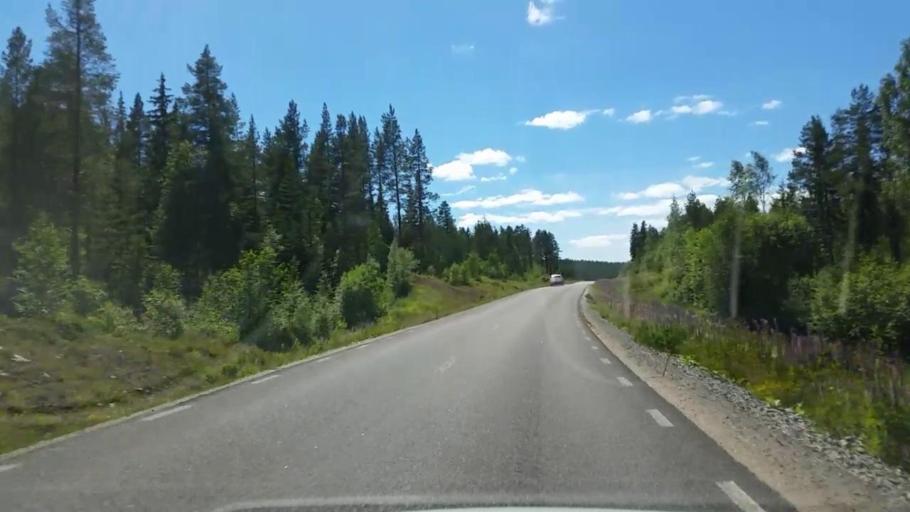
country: SE
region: Gaevleborg
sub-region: Ljusdals Kommun
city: Farila
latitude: 61.6346
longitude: 15.5839
